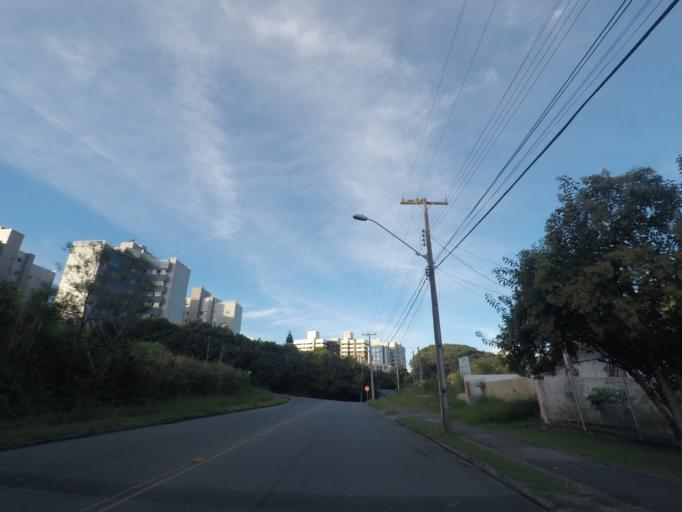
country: BR
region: Parana
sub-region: Curitiba
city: Curitiba
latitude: -25.4022
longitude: -49.2569
